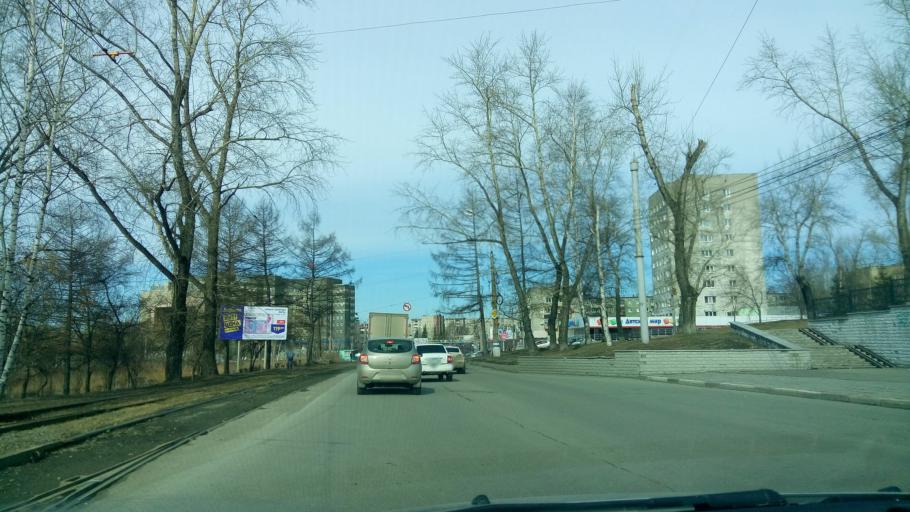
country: RU
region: Sverdlovsk
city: Nizhniy Tagil
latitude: 57.9065
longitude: 59.9496
